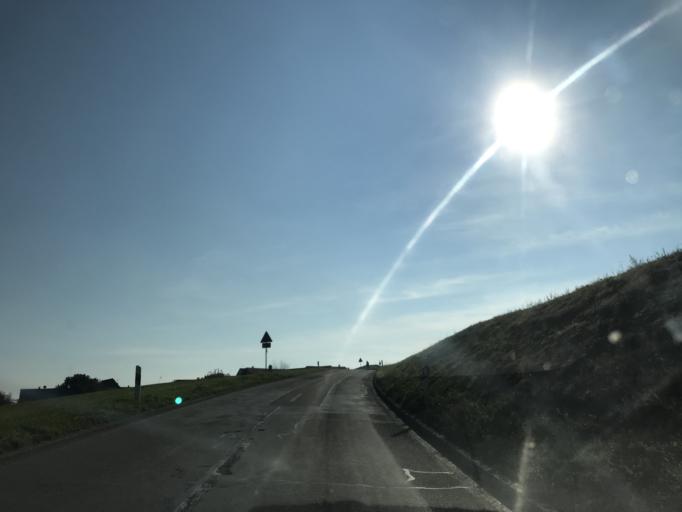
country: DE
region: Baden-Wuerttemberg
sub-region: Freiburg Region
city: Gorwihl
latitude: 47.6229
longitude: 8.0514
